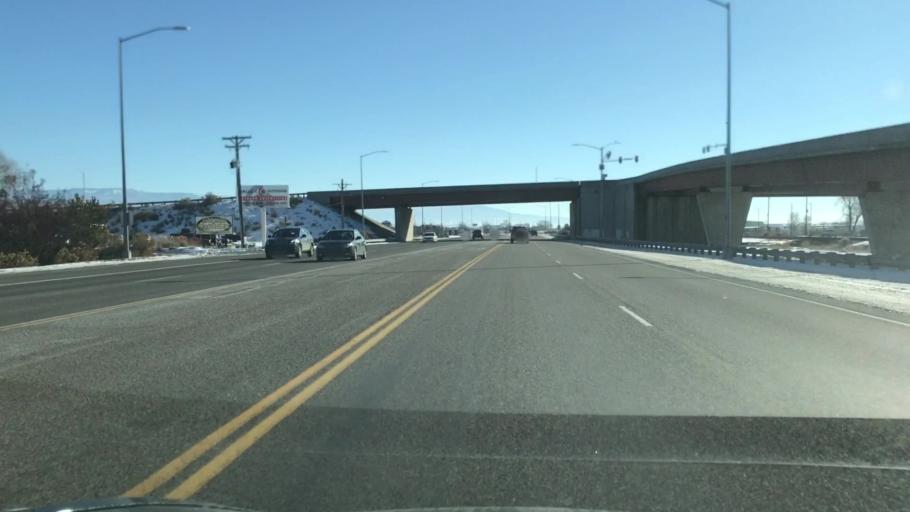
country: US
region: Colorado
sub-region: Mesa County
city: Redlands
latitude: 39.0924
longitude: -108.6103
